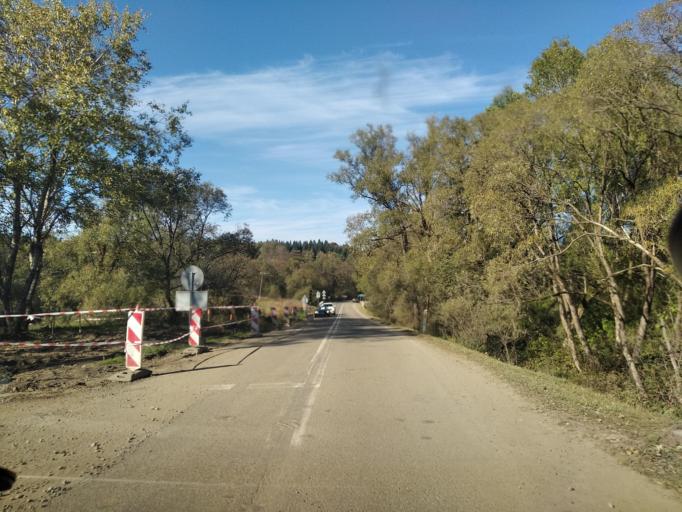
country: PL
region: Subcarpathian Voivodeship
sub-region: Powiat leski
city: Cisna
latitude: 49.2634
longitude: 22.2878
